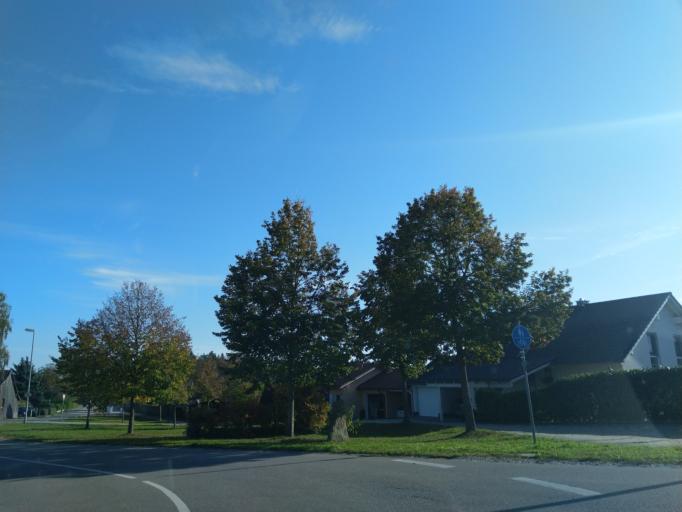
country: DE
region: Bavaria
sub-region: Lower Bavaria
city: Metten
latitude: 48.8821
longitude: 12.8961
